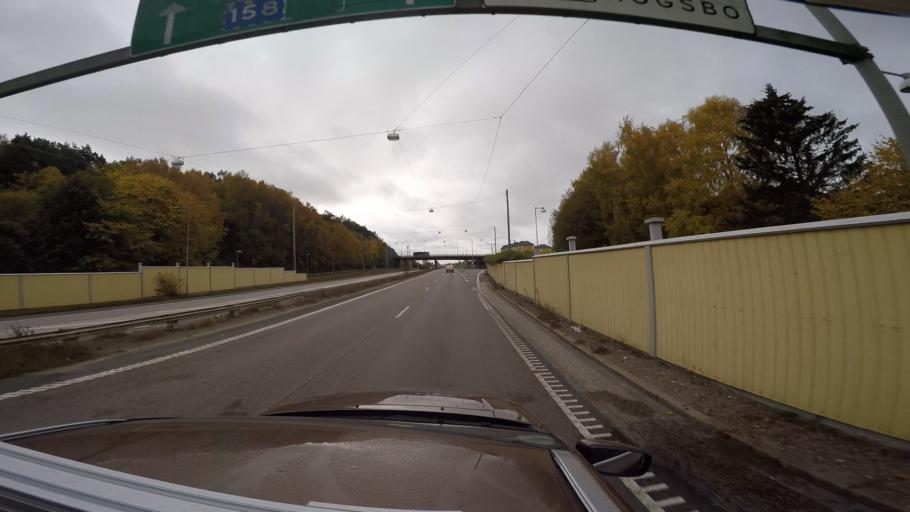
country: SE
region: Vaestra Goetaland
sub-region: Goteborg
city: Majorna
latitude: 57.6739
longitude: 11.9393
